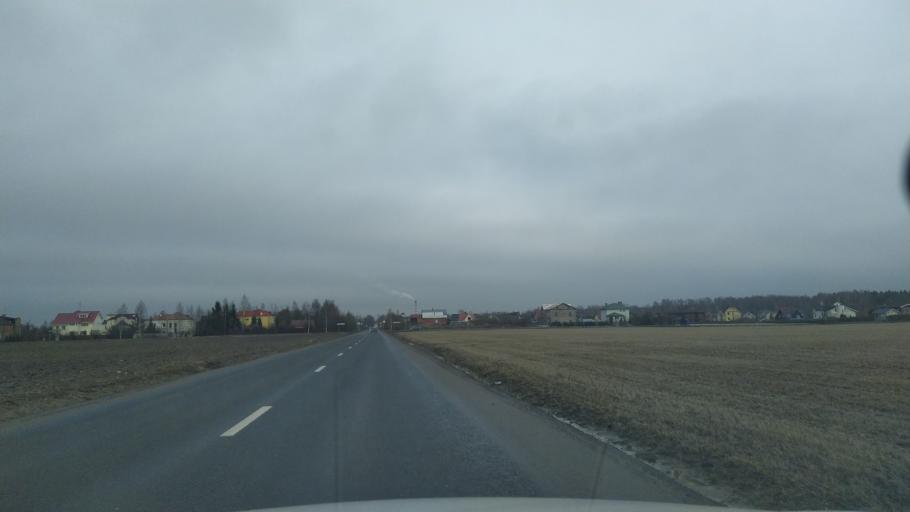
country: RU
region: St.-Petersburg
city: Aleksandrovskaya
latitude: 59.7204
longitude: 30.3435
